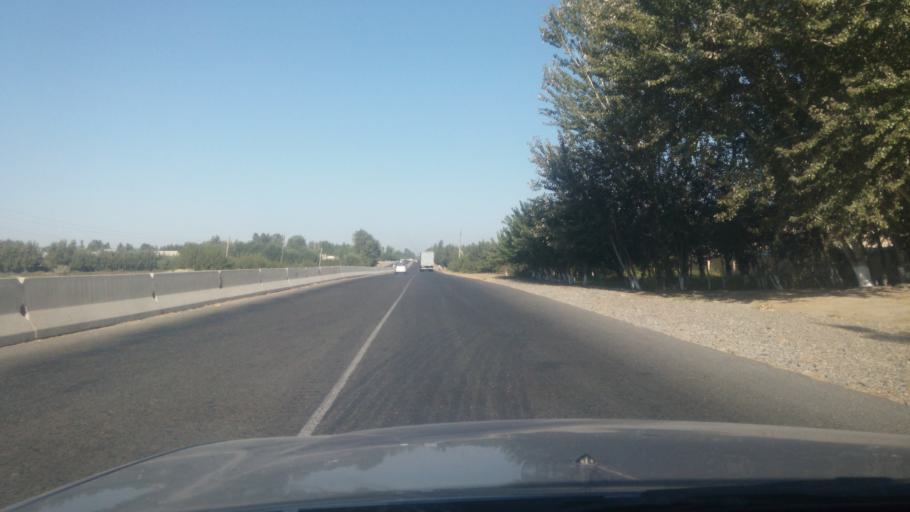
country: UZ
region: Samarqand
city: Oqtosh
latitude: 39.9442
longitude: 66.0266
